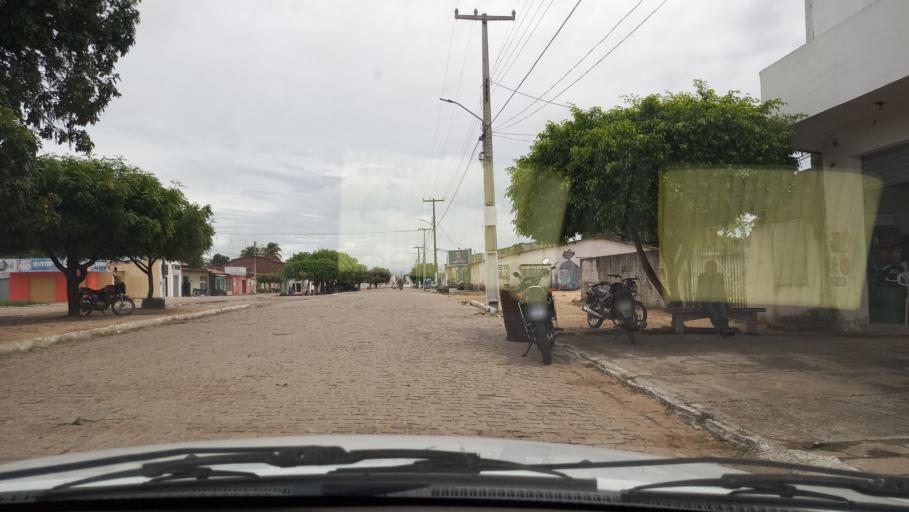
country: BR
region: Rio Grande do Norte
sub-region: Poco Branco
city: Poco Branco
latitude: -5.6203
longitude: -35.6643
